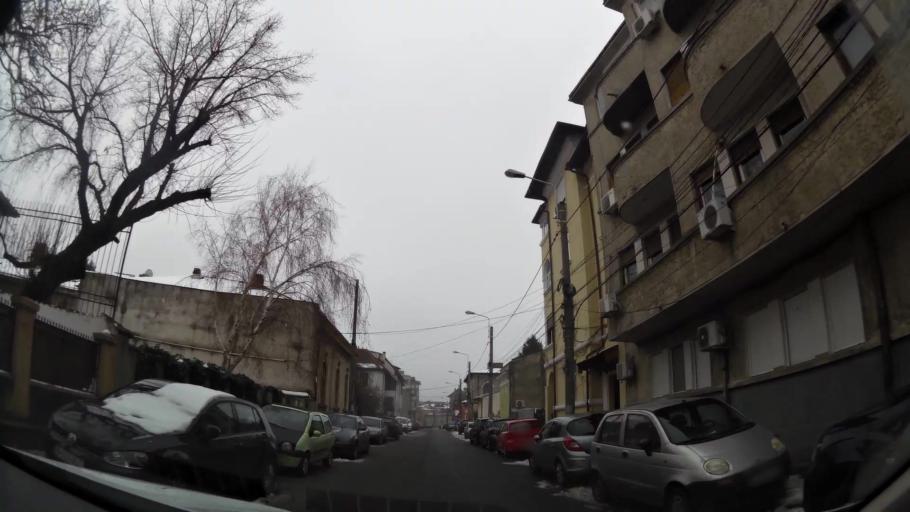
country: RO
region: Bucuresti
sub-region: Municipiul Bucuresti
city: Bucharest
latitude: 44.4379
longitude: 26.1226
